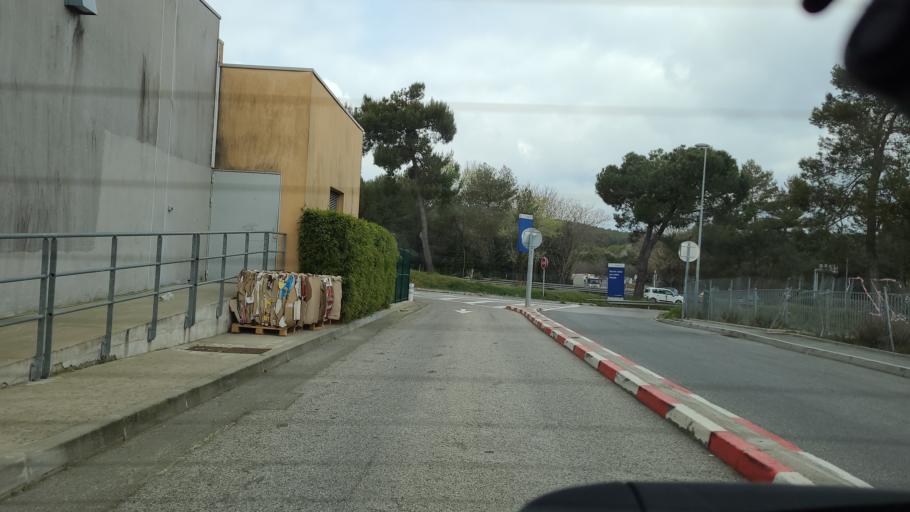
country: FR
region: Provence-Alpes-Cote d'Azur
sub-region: Departement des Alpes-Maritimes
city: Le Cannet
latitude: 43.5897
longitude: 7.0356
